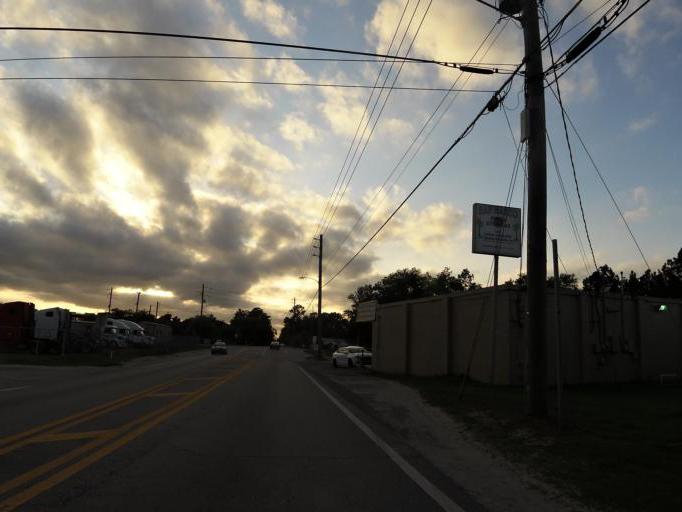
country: US
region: Florida
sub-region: Duval County
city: Jacksonville
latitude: 30.4435
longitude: -81.6118
